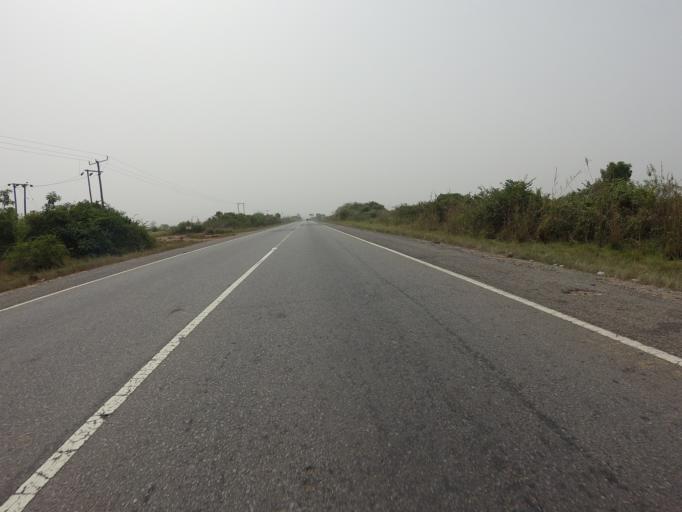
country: GH
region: Volta
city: Anloga
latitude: 5.9746
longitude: 0.5248
